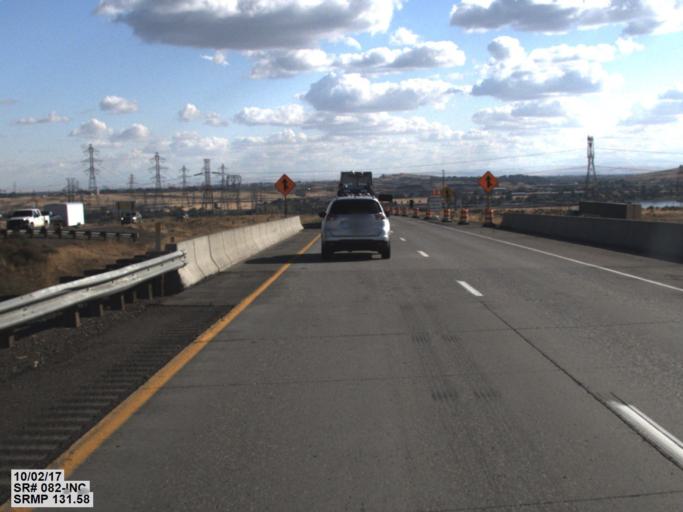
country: US
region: Oregon
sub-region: Umatilla County
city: Umatilla
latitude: 45.9458
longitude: -119.3356
